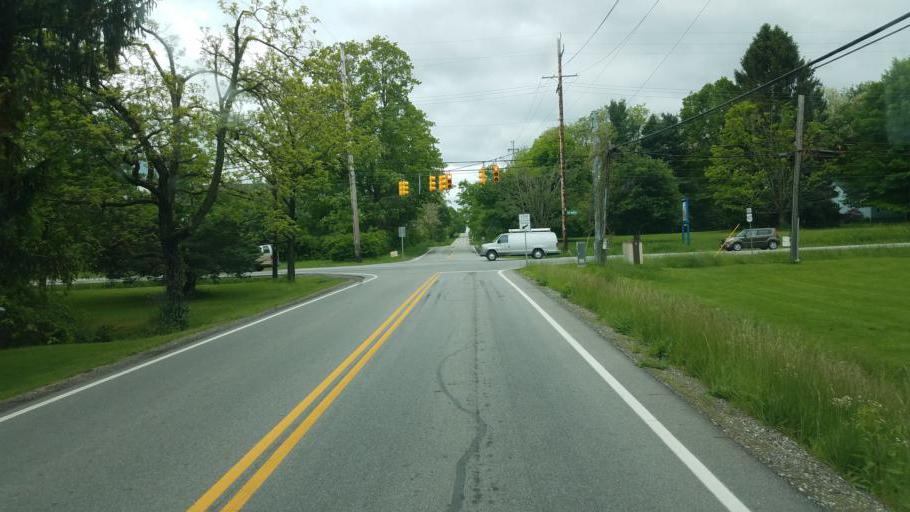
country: US
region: Ohio
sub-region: Portage County
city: Hiram
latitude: 41.3875
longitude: -81.1717
